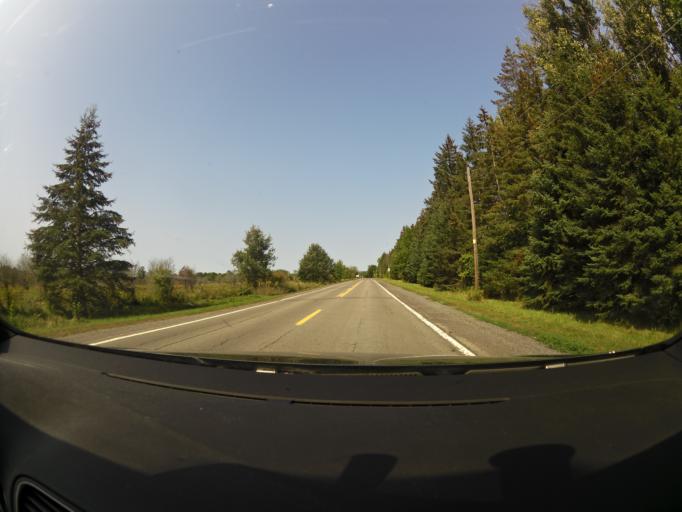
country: CA
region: Ontario
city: Arnprior
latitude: 45.5082
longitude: -76.2169
